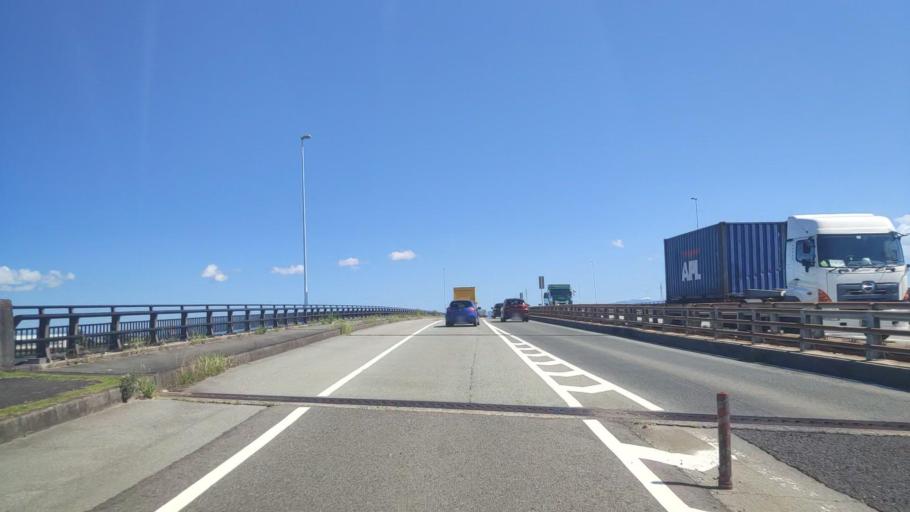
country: JP
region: Mie
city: Hisai-motomachi
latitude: 34.6131
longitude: 136.5181
